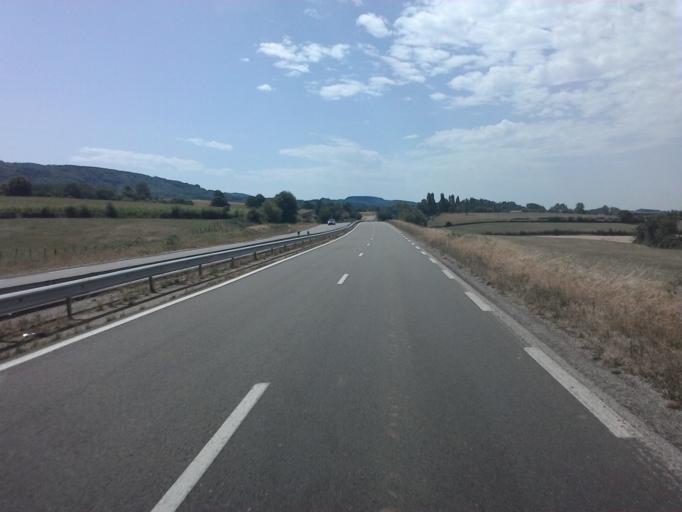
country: FR
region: Bourgogne
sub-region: Departement de Saone-et-Loire
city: Cuiseaux
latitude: 46.5090
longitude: 5.3876
